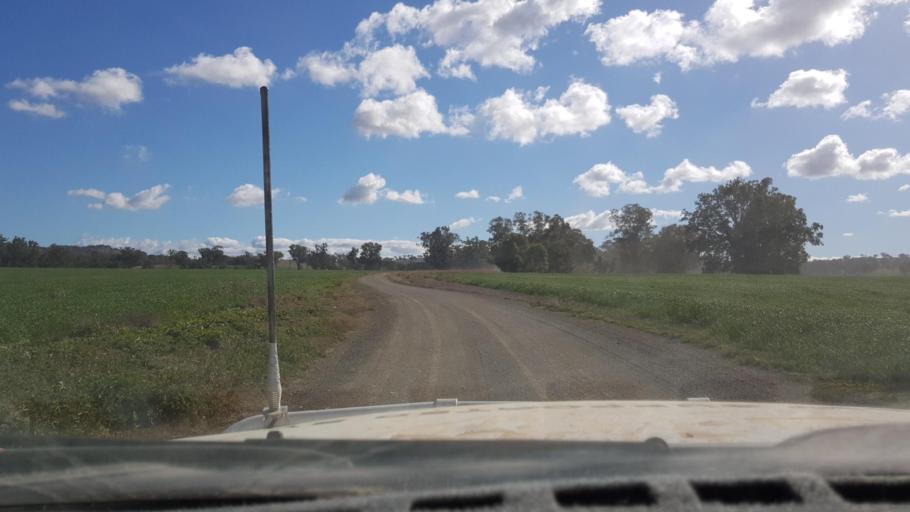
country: AU
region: New South Wales
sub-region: Narrabri
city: Blair Athol
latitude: -30.5799
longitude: 150.4729
